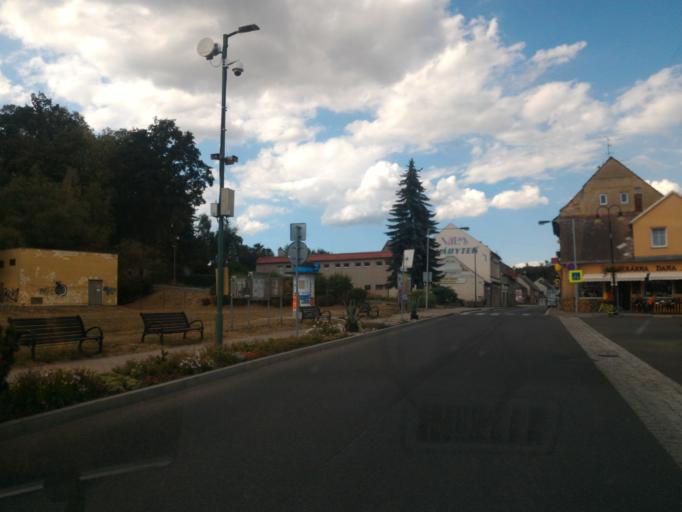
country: CZ
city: Mimon
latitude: 50.6589
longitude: 14.7247
